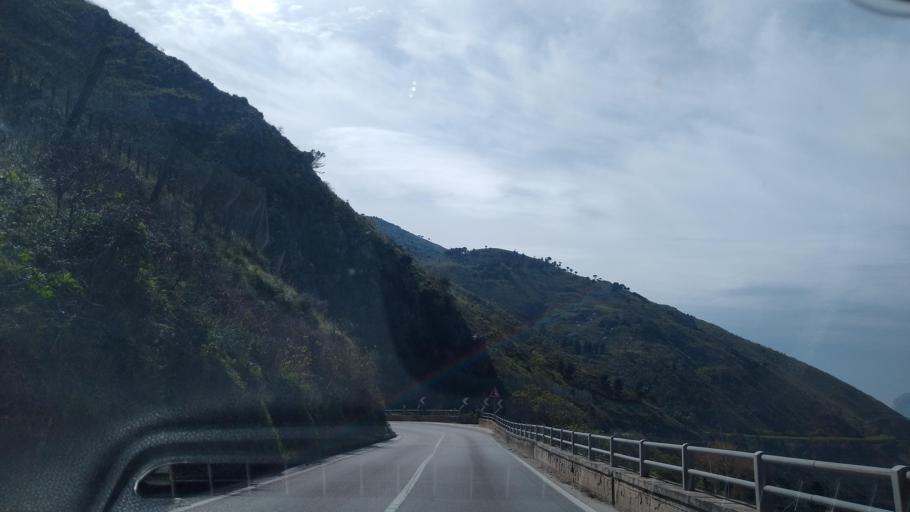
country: IT
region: Sicily
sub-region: Palermo
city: Pioppo
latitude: 38.0502
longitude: 13.1906
